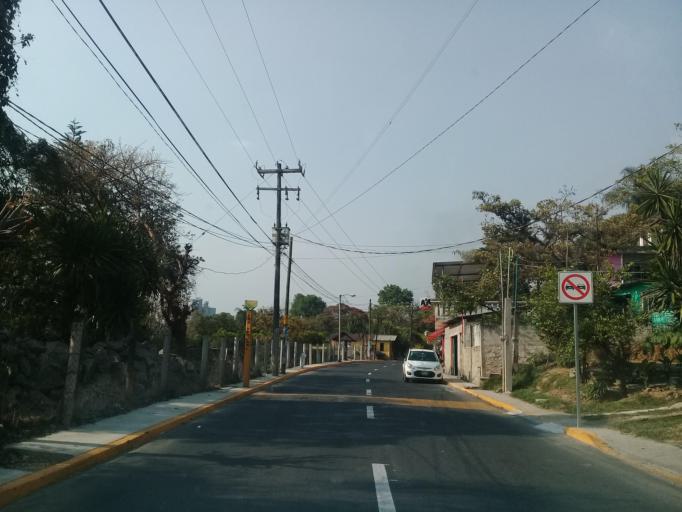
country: MX
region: Veracruz
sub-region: Ixtaczoquitlan
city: Campo Chico
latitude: 18.8482
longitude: -97.0367
